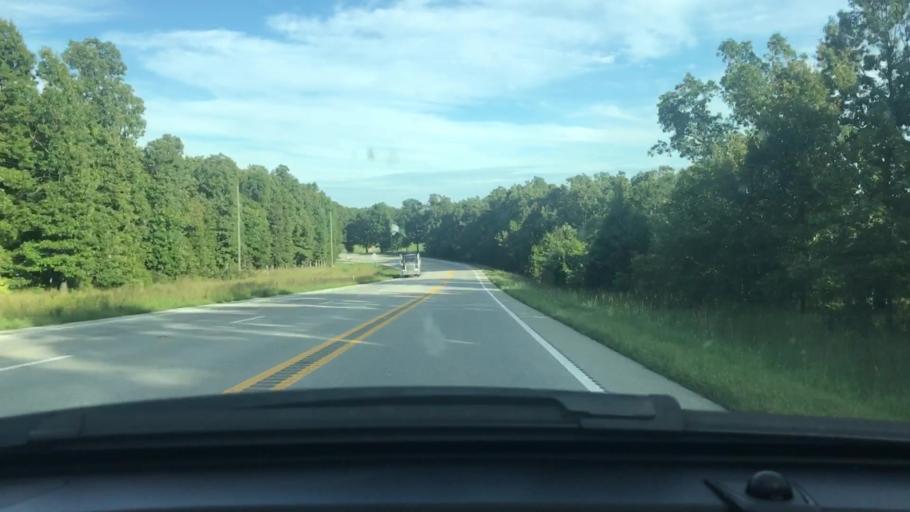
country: US
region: Arkansas
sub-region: Sharp County
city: Cherokee Village
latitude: 36.2726
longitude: -91.3720
